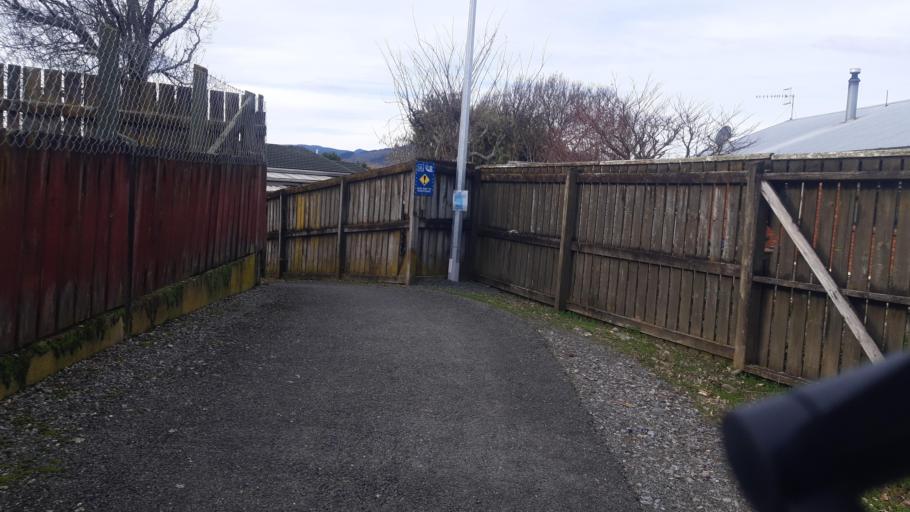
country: NZ
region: Tasman
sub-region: Tasman District
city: Brightwater
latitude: -41.3770
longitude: 173.1075
